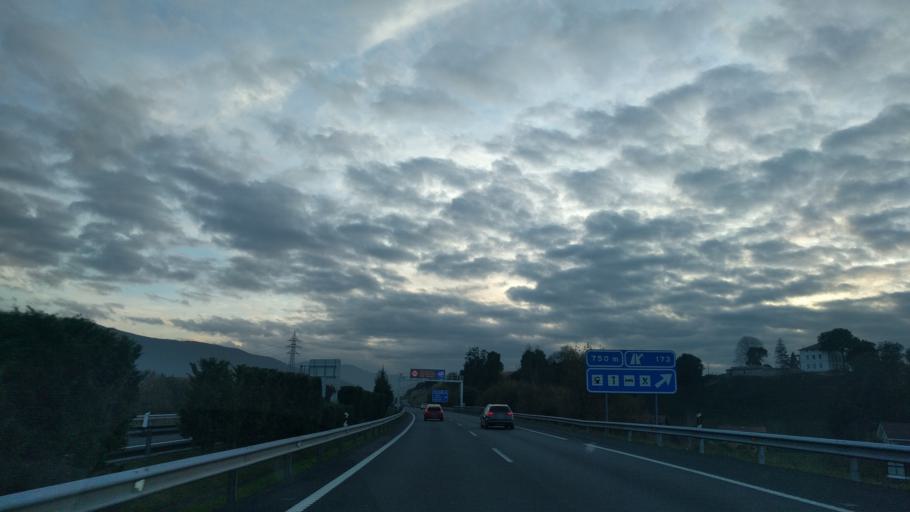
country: ES
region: Cantabria
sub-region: Provincia de Cantabria
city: Colindres
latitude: 43.3957
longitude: -3.4425
